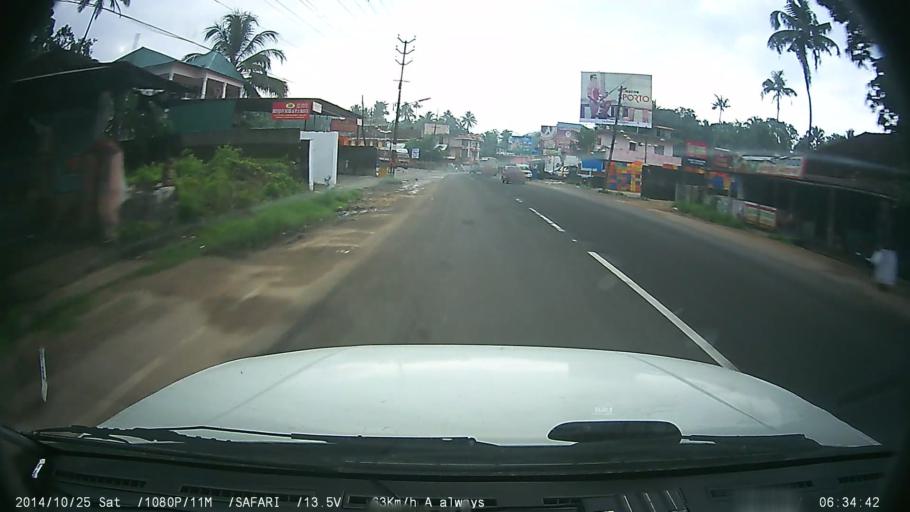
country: IN
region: Kerala
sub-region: Ernakulam
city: Muvattupula
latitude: 10.0069
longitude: 76.5697
